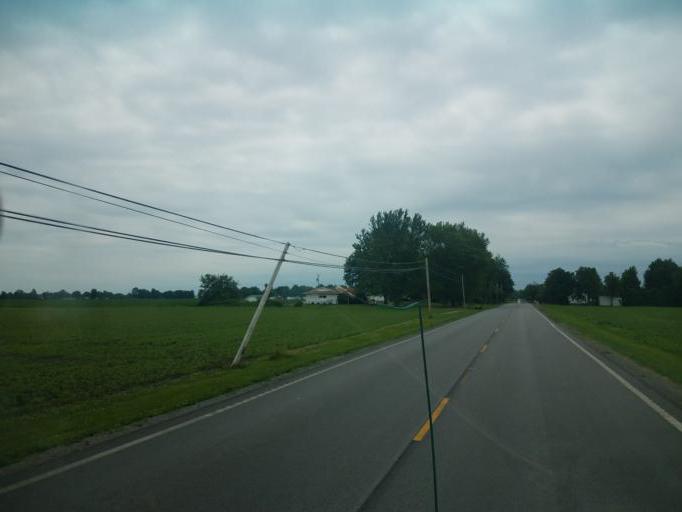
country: US
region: Ohio
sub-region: Hardin County
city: Ada
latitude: 40.7863
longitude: -83.8232
